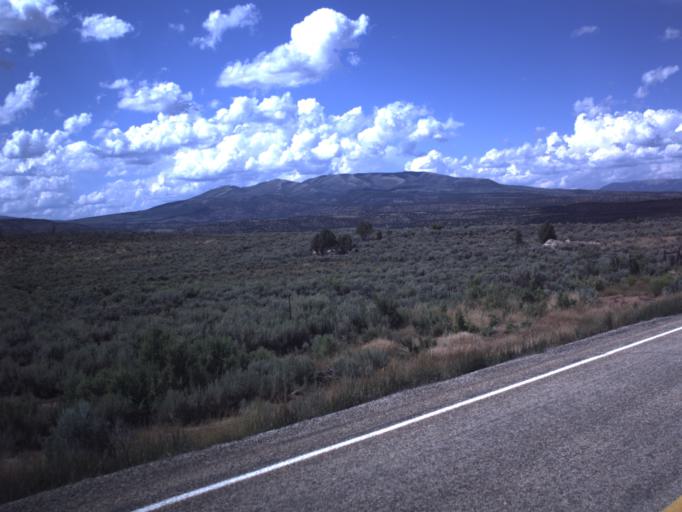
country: US
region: Utah
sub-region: Duchesne County
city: Duchesne
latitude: 40.2088
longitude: -110.7302
